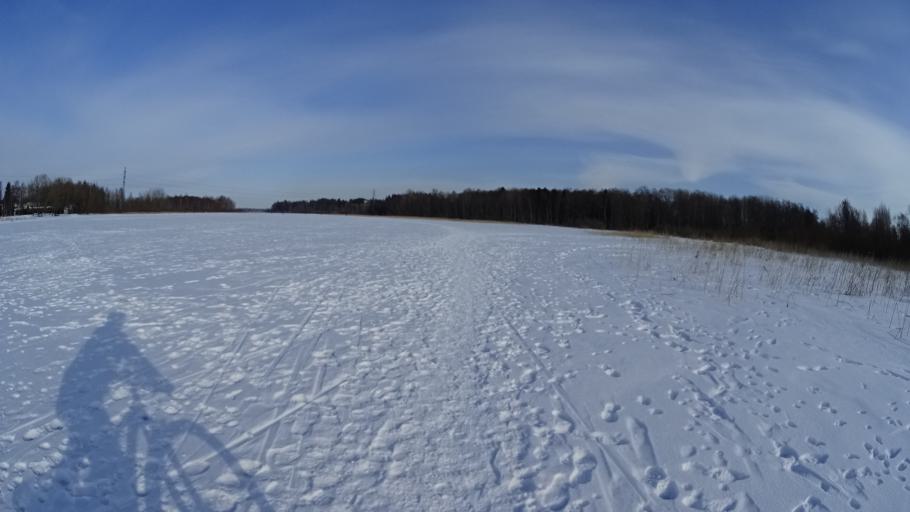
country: FI
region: Uusimaa
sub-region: Helsinki
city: Kauniainen
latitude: 60.2391
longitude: 24.7212
